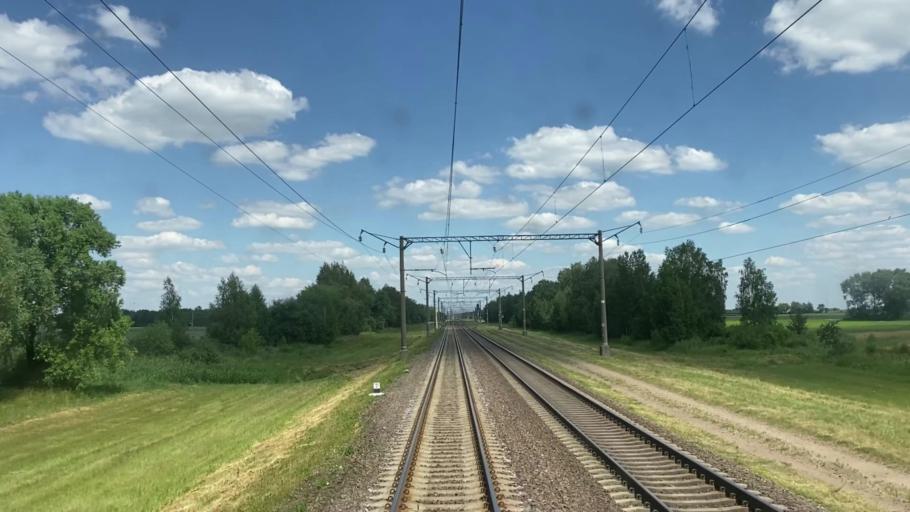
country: BY
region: Brest
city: Charnawchytsy
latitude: 52.1372
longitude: 23.8317
